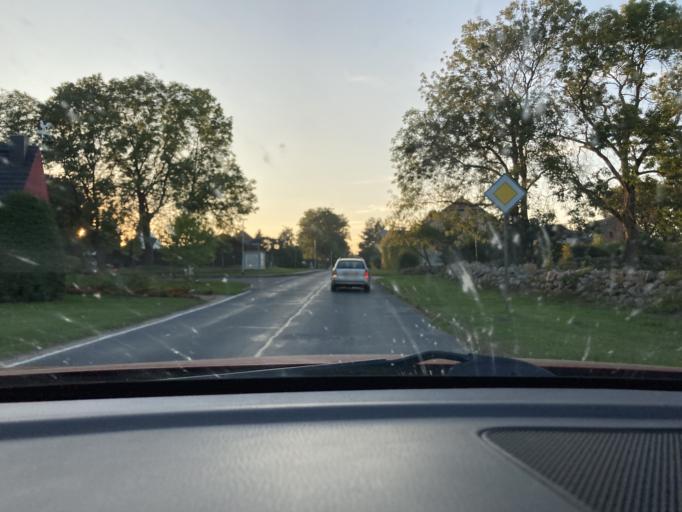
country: DE
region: Mecklenburg-Vorpommern
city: Alt-Sanitz
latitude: 53.7511
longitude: 13.6289
